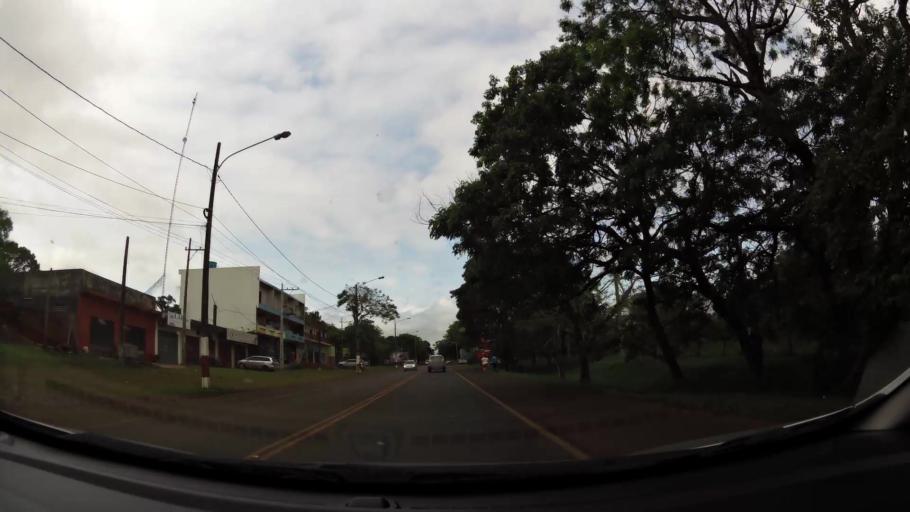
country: PY
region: Alto Parana
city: Ciudad del Este
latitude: -25.4103
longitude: -54.6330
